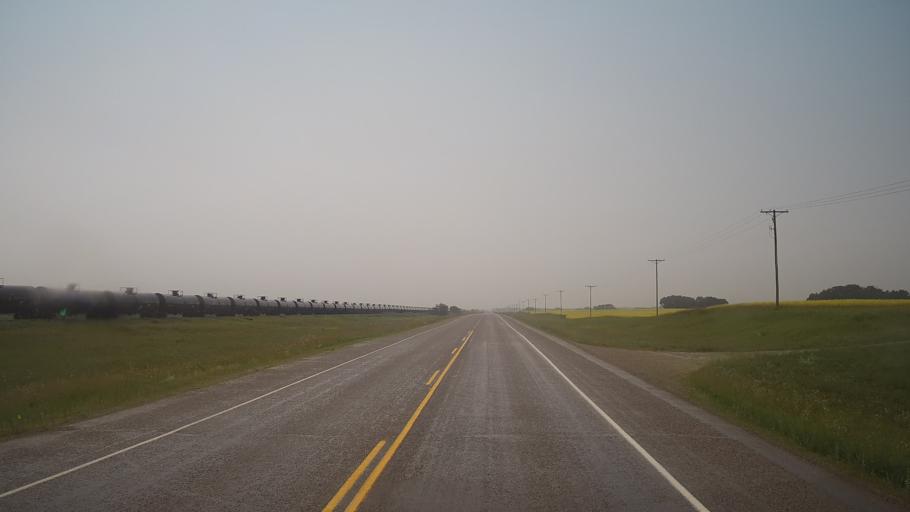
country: CA
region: Saskatchewan
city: Biggar
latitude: 52.1576
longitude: -108.2642
